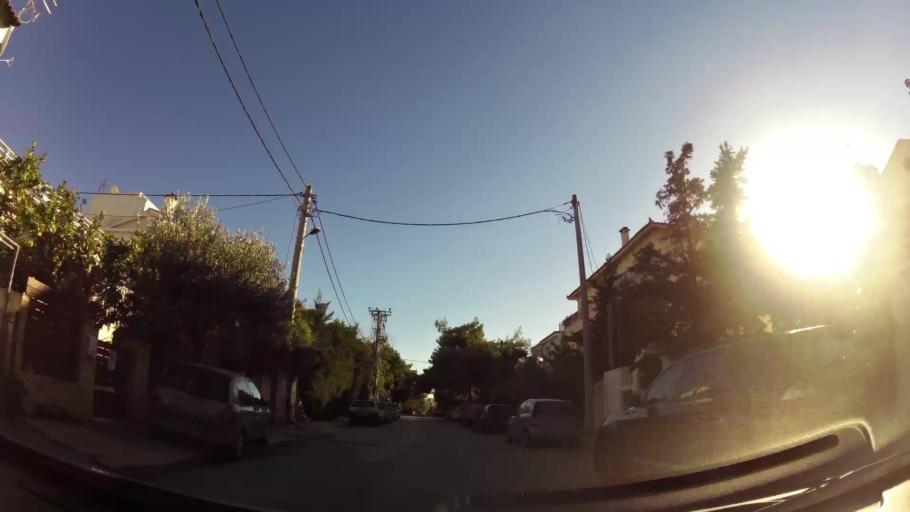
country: GR
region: Attica
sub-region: Nomarchia Athinas
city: Kifisia
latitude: 38.0867
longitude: 23.8057
